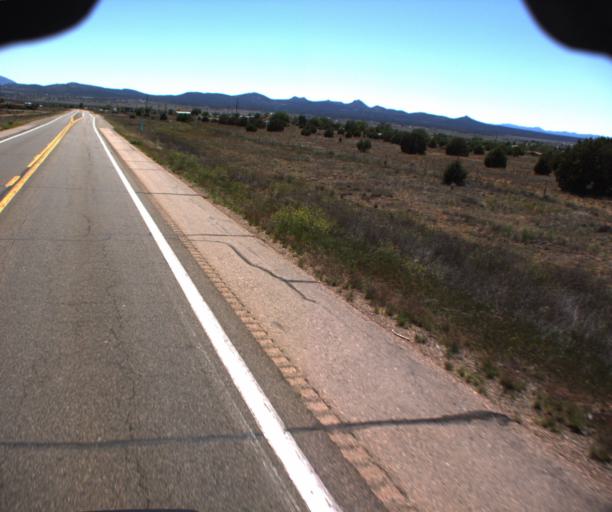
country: US
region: Arizona
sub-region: Yavapai County
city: Paulden
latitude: 34.9137
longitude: -112.4583
